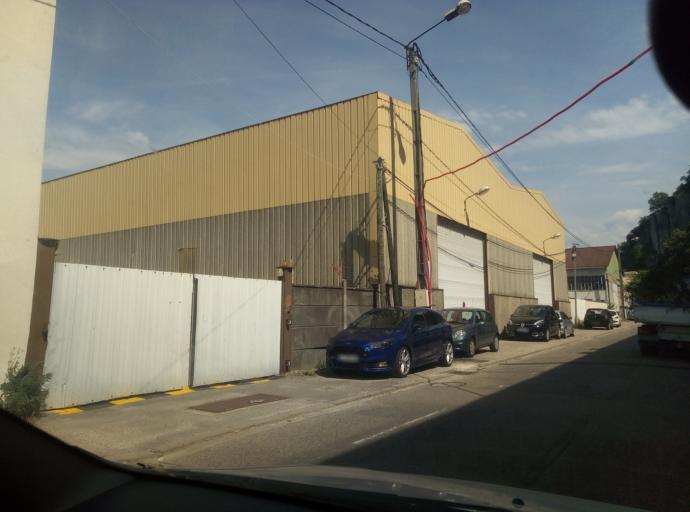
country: FR
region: Rhone-Alpes
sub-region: Departement de l'Isere
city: Fontaine
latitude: 45.1863
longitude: 5.6839
